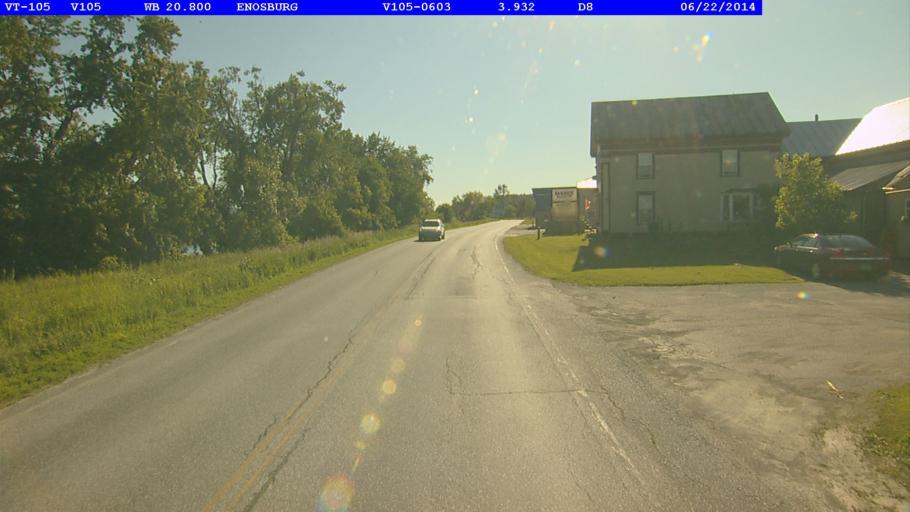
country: US
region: Vermont
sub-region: Franklin County
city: Enosburg Falls
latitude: 44.9211
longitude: -72.7502
